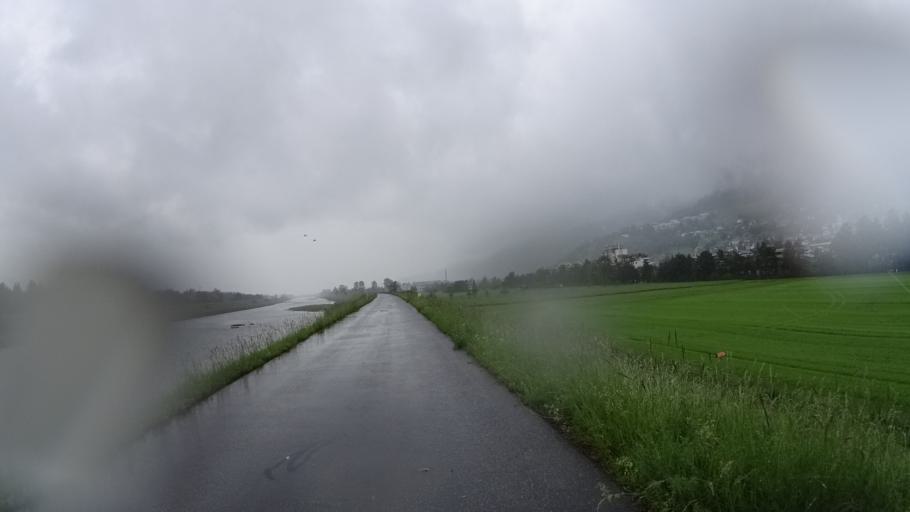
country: LI
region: Triesen
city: Triesen
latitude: 47.0998
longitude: 9.5206
